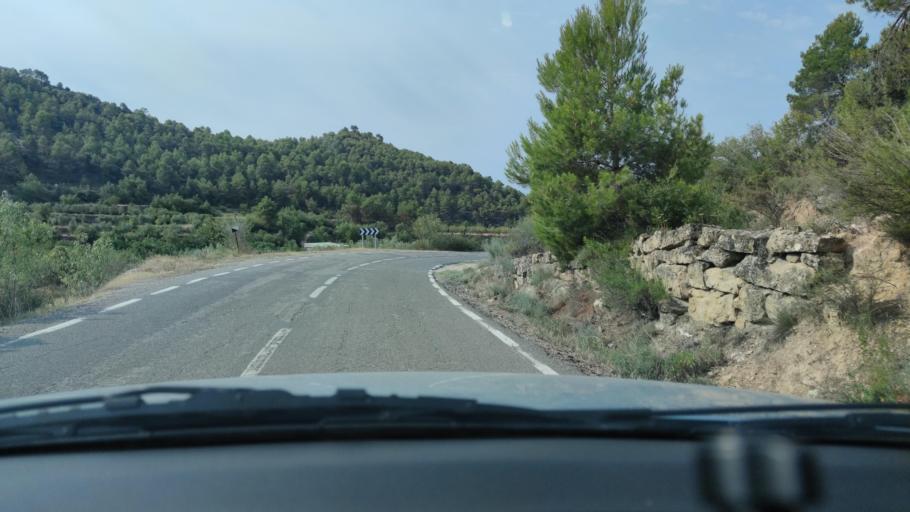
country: ES
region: Catalonia
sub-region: Provincia de Lleida
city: Juncosa
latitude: 41.4352
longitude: 0.8641
